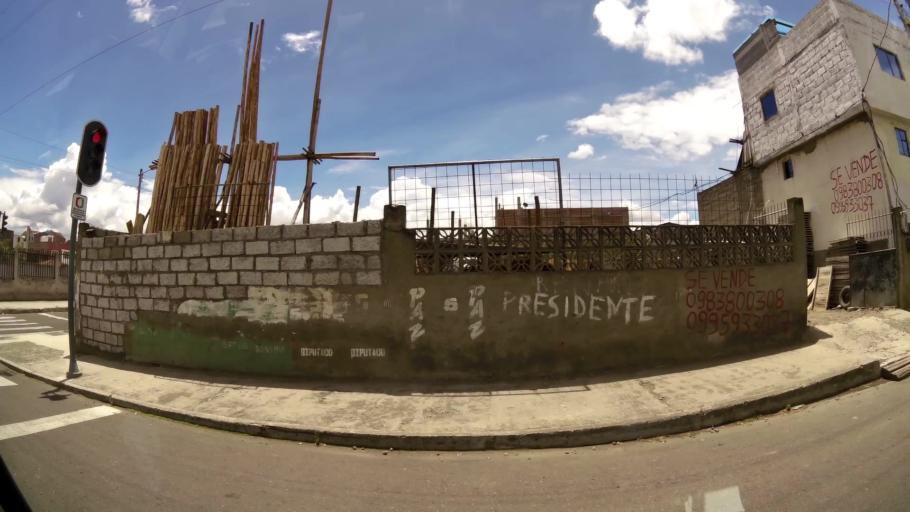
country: EC
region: Tungurahua
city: Ambato
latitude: -1.2651
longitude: -78.6108
